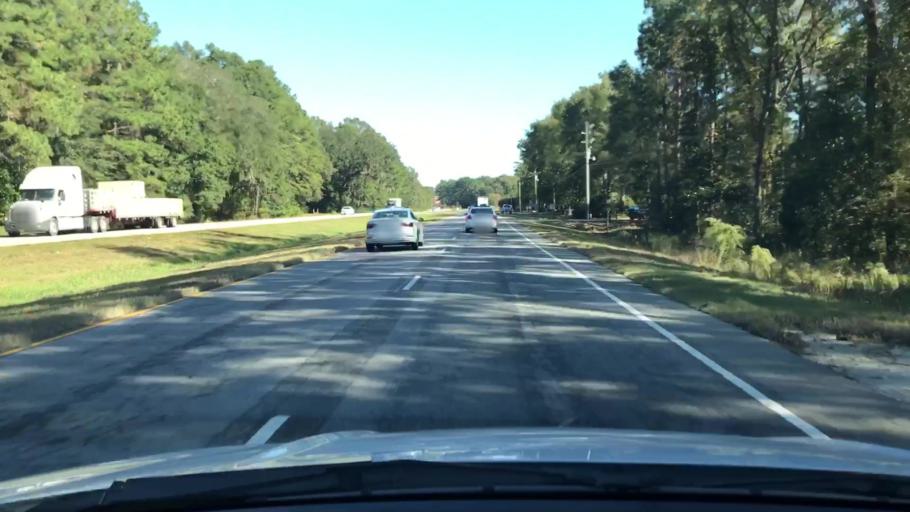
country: US
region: South Carolina
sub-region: Charleston County
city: Ravenel
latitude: 32.7807
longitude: -80.1863
